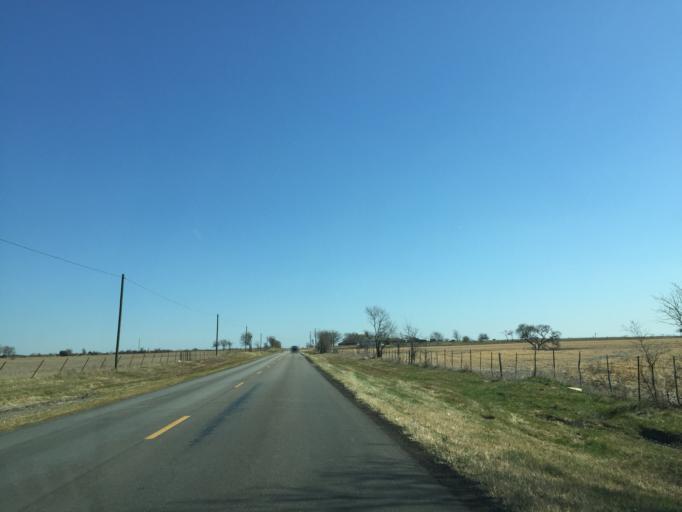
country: US
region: Texas
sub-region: Williamson County
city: Serenada
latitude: 30.7350
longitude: -97.6063
